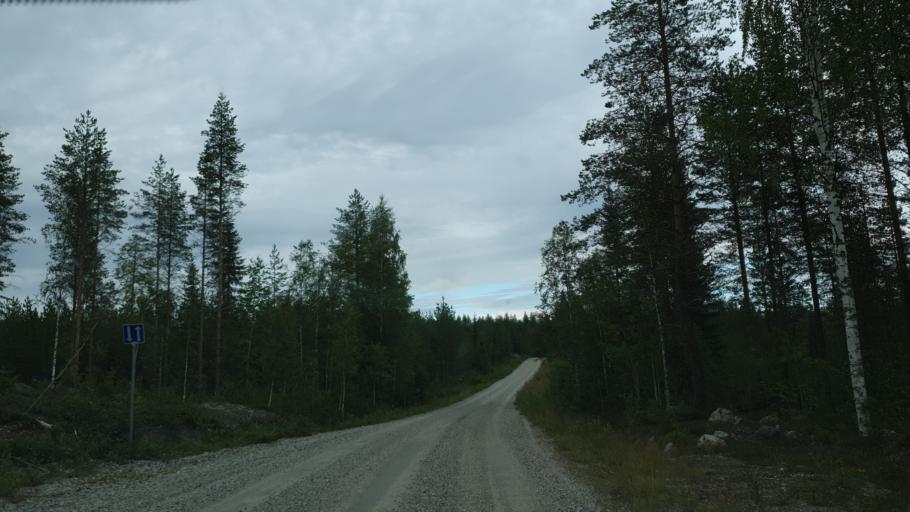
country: FI
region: Kainuu
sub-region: Kehys-Kainuu
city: Kuhmo
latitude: 64.4500
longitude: 29.5612
